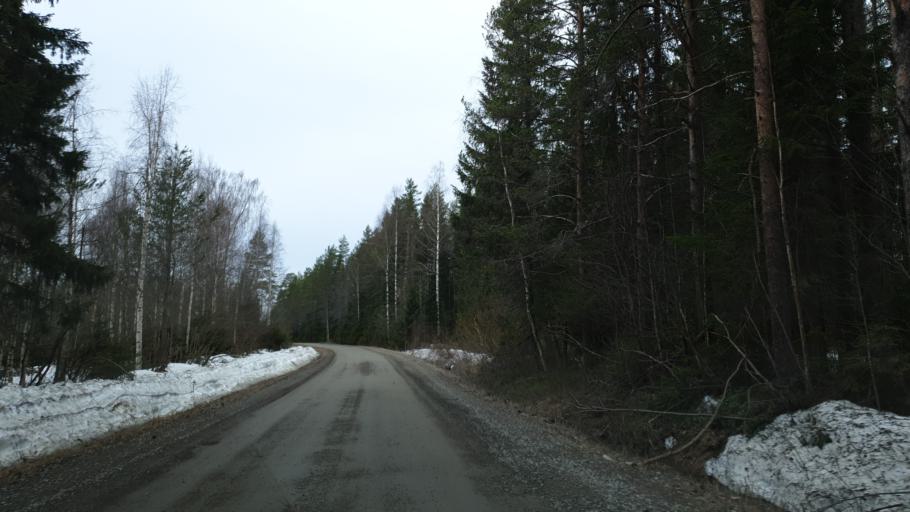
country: SE
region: Vaesterbotten
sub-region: Robertsfors Kommun
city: Robertsfors
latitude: 64.3860
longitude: 20.9332
